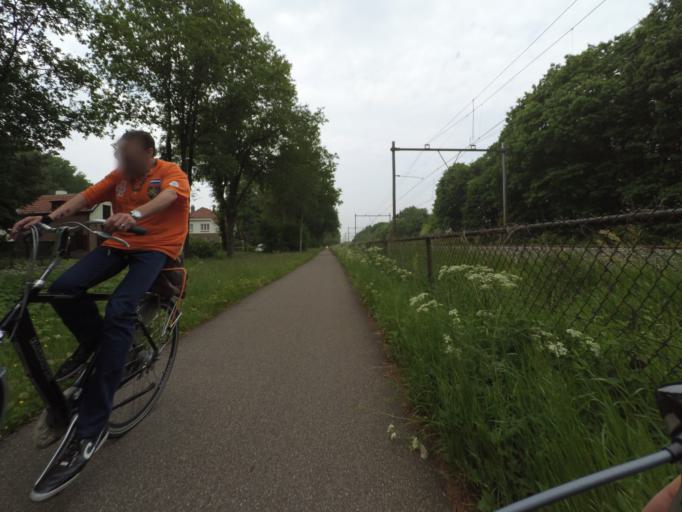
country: NL
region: Gelderland
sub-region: Gemeente Renkum
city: Wolfheze
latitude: 52.0076
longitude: 5.7814
